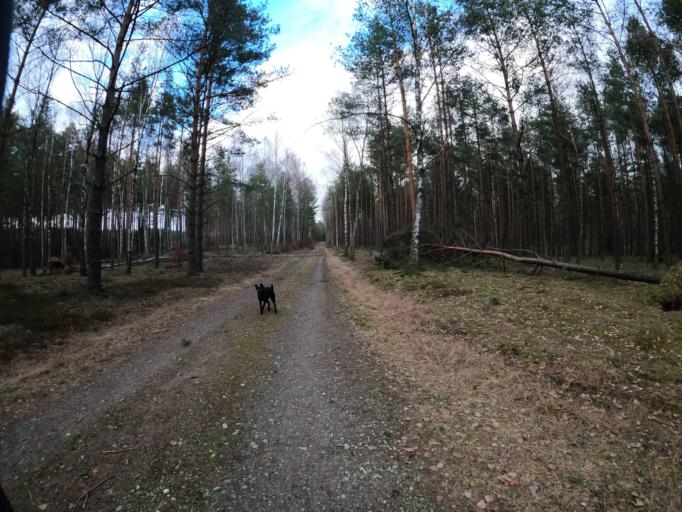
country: PL
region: Greater Poland Voivodeship
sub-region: Powiat zlotowski
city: Sypniewo
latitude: 53.4396
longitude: 16.5824
